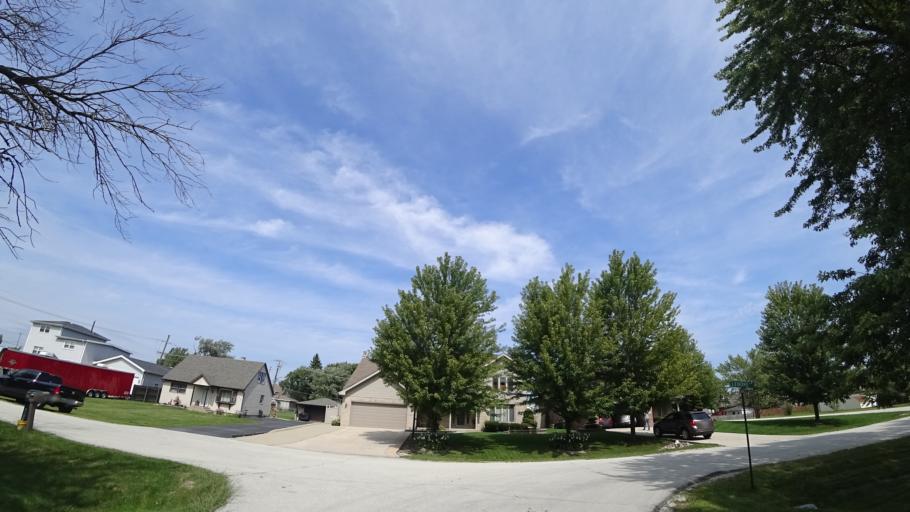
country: US
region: Illinois
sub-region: Cook County
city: Orland Hills
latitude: 41.5565
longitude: -87.8457
